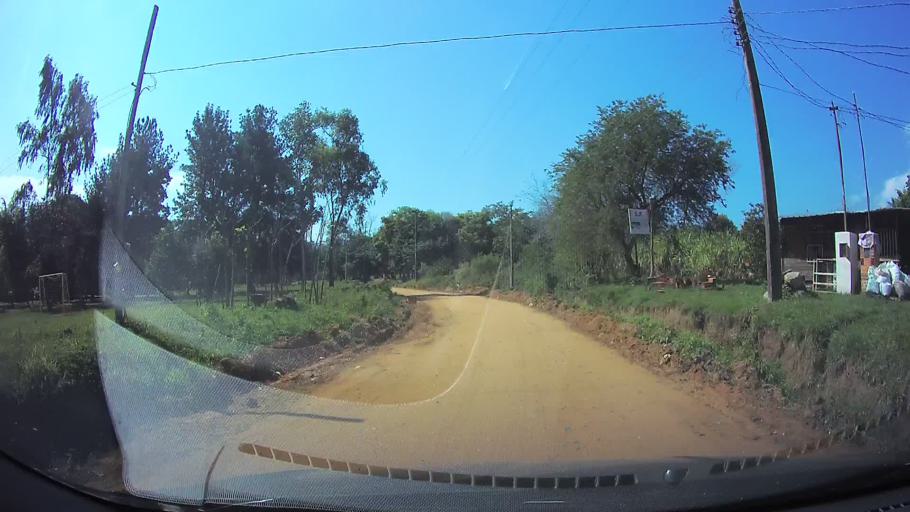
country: PY
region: Central
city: Limpio
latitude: -25.2292
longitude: -57.4406
